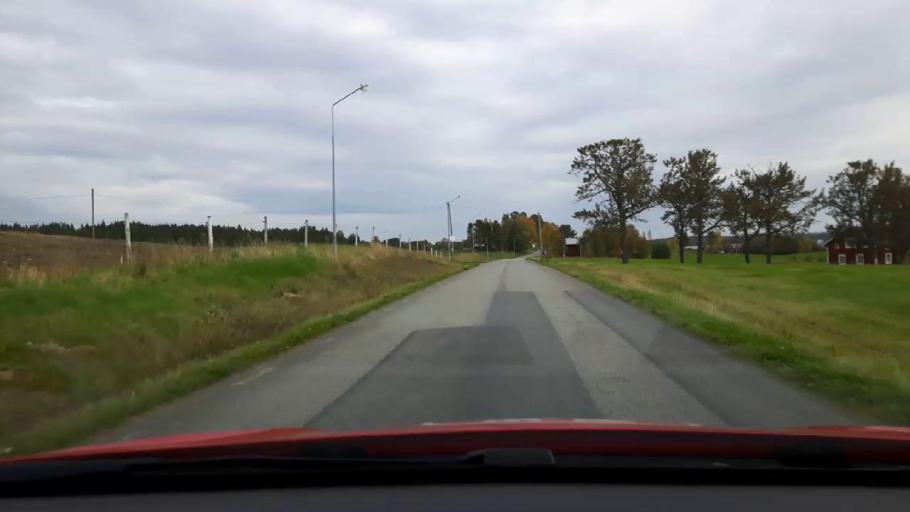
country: SE
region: Jaemtland
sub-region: Krokoms Kommun
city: Valla
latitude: 63.2525
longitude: 14.0315
